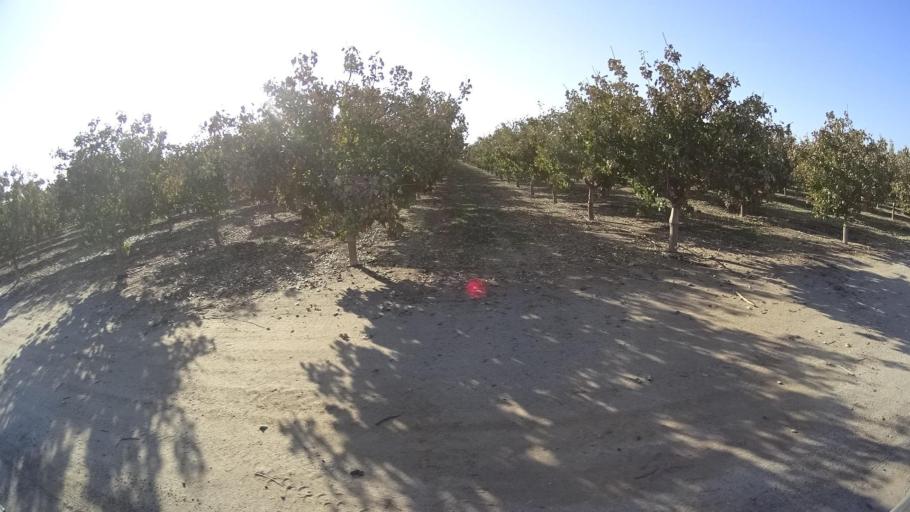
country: US
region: California
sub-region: Tulare County
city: Richgrove
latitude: 35.7327
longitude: -119.1181
